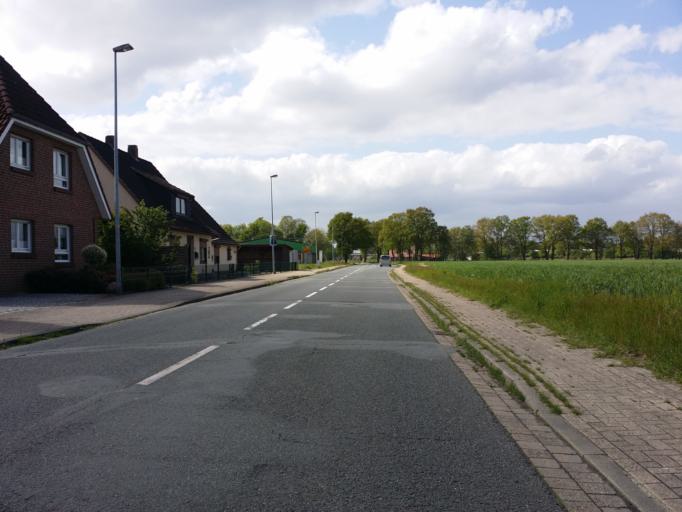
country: DE
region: Lower Saxony
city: Kirchseelte
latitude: 53.0019
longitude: 8.7017
